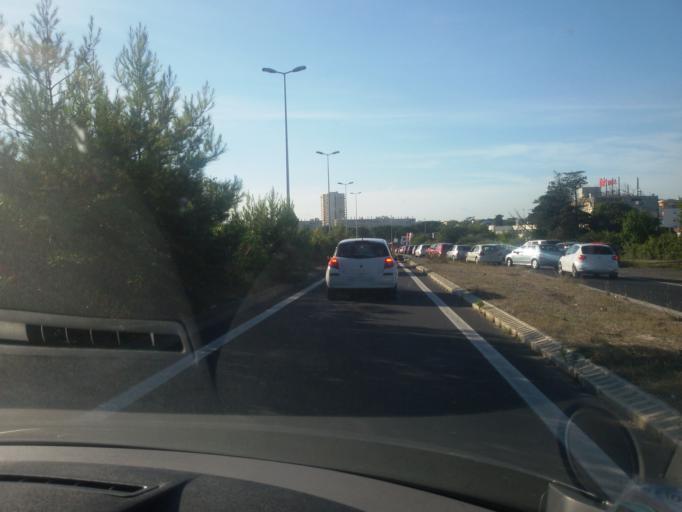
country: FR
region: Languedoc-Roussillon
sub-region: Departement de l'Herault
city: Lattes
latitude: 43.5878
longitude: 3.8930
